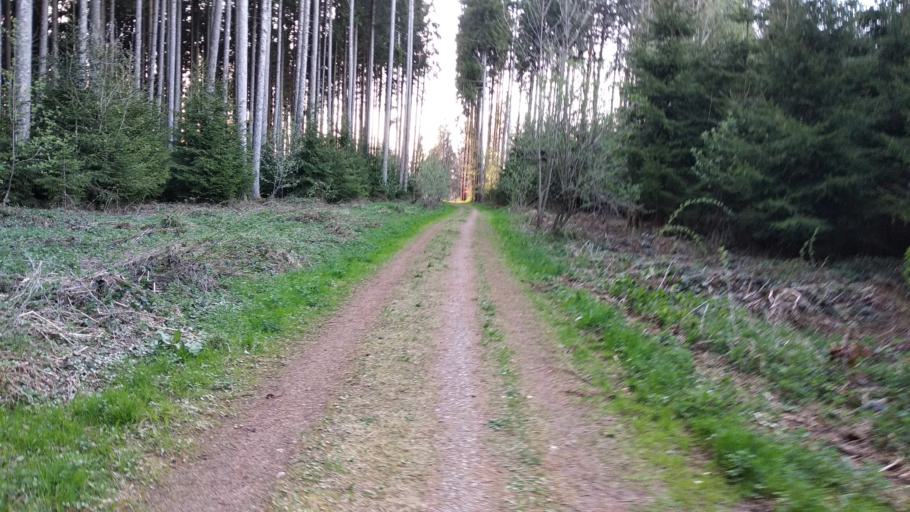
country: DE
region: Bavaria
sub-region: Swabia
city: Lautrach
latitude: 47.8958
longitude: 10.1249
